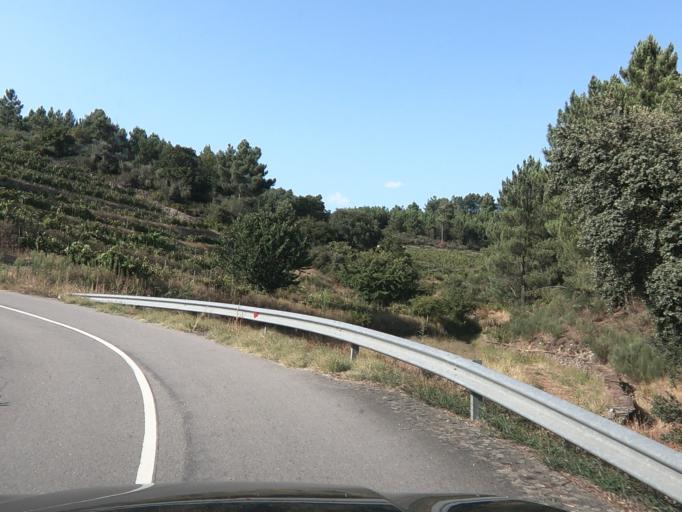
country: PT
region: Vila Real
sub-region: Sabrosa
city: Vilela
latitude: 41.2217
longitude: -7.6262
